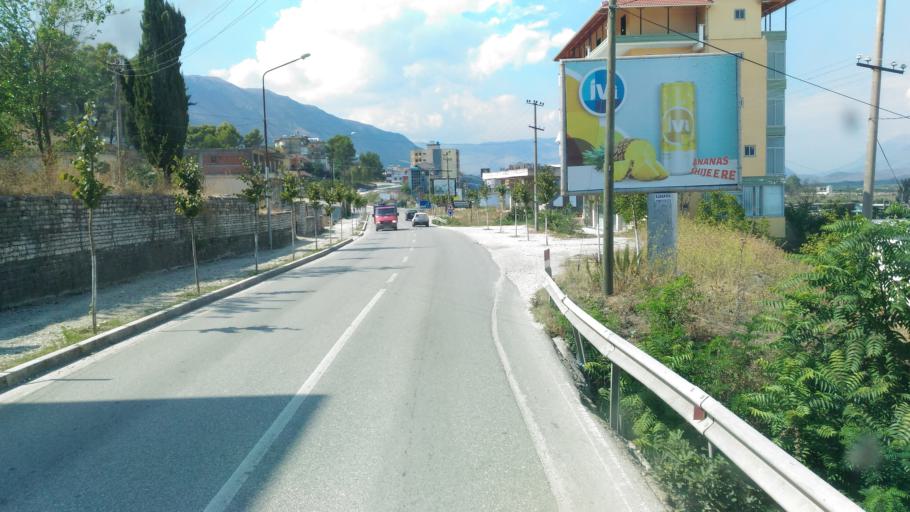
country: AL
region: Gjirokaster
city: Gjirokaster
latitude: 40.0761
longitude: 20.1530
